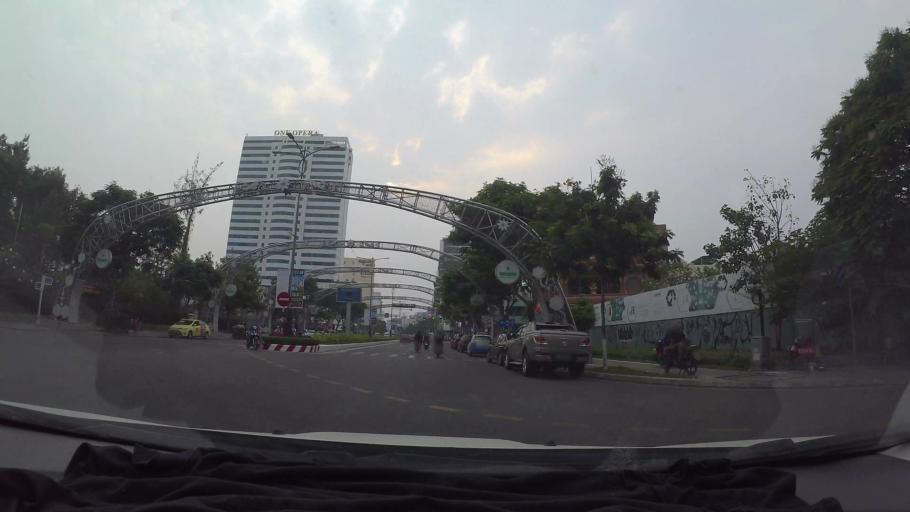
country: VN
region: Da Nang
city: Da Nang
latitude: 16.0609
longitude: 108.2183
